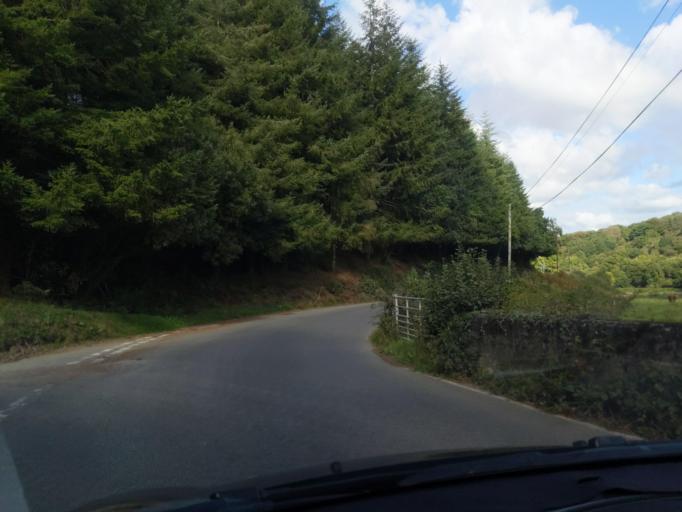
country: GB
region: England
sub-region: Devon
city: Great Torrington
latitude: 50.9352
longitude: -4.1851
